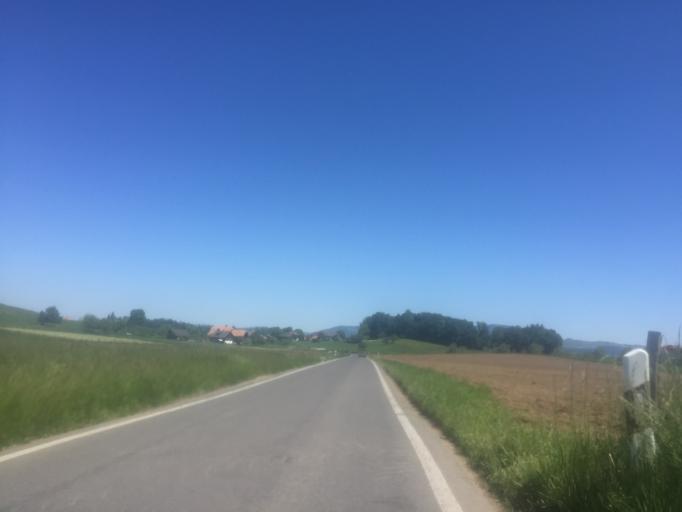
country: CH
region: Bern
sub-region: Thun District
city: Thierachern
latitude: 46.7446
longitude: 7.5628
